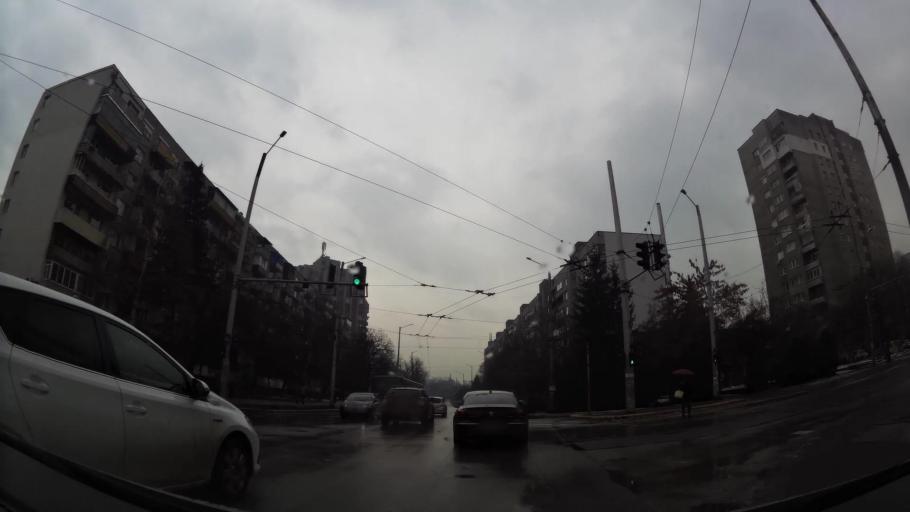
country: BG
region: Sofia-Capital
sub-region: Stolichna Obshtina
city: Sofia
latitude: 42.6668
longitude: 23.3006
